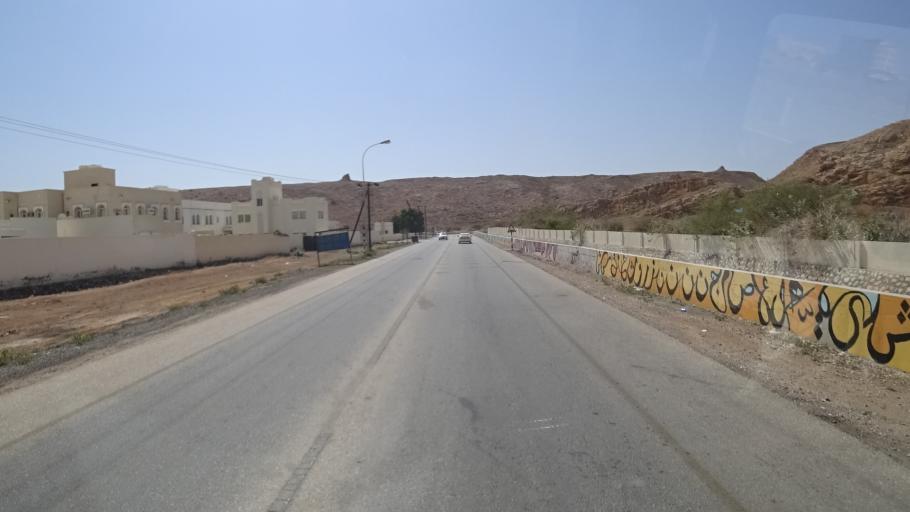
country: OM
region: Ash Sharqiyah
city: Sur
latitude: 22.5633
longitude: 59.5437
